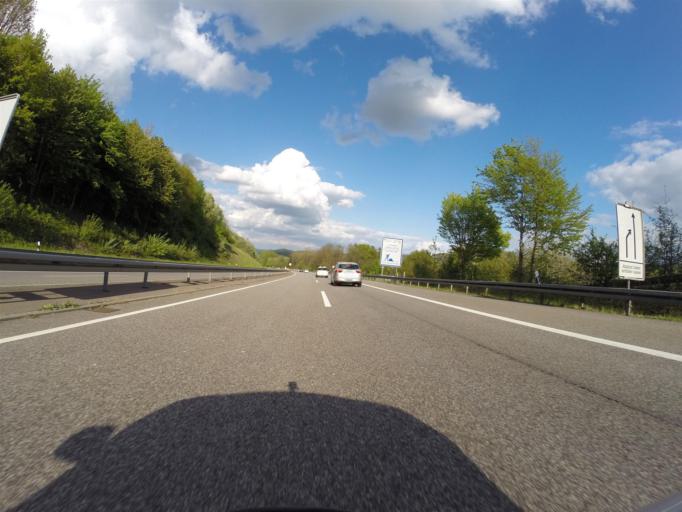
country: DE
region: Saarland
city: Orscholz
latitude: 49.4516
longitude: 6.5395
